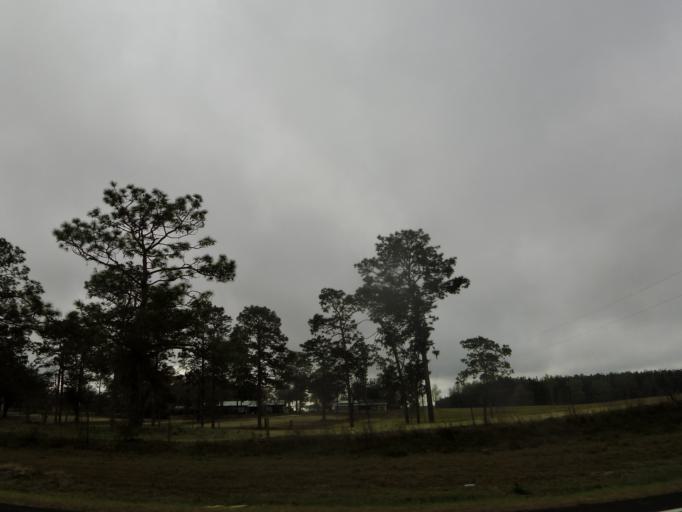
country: US
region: Florida
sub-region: Alachua County
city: High Springs
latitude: 29.8154
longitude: -82.7023
